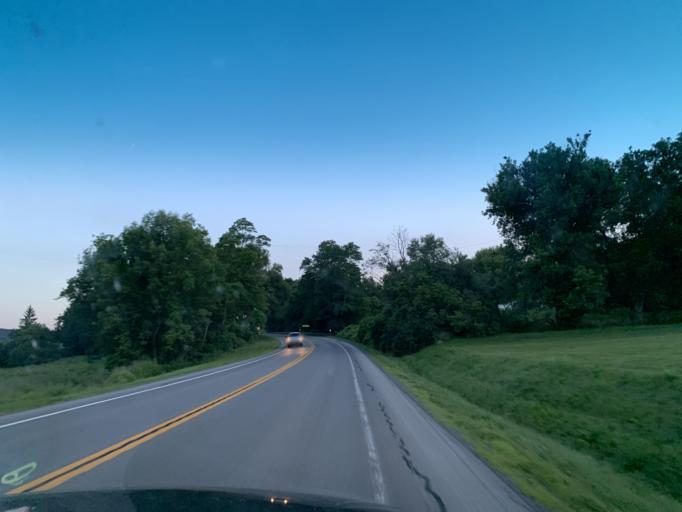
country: US
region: New York
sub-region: Chenango County
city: New Berlin
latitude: 42.7660
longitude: -75.2797
